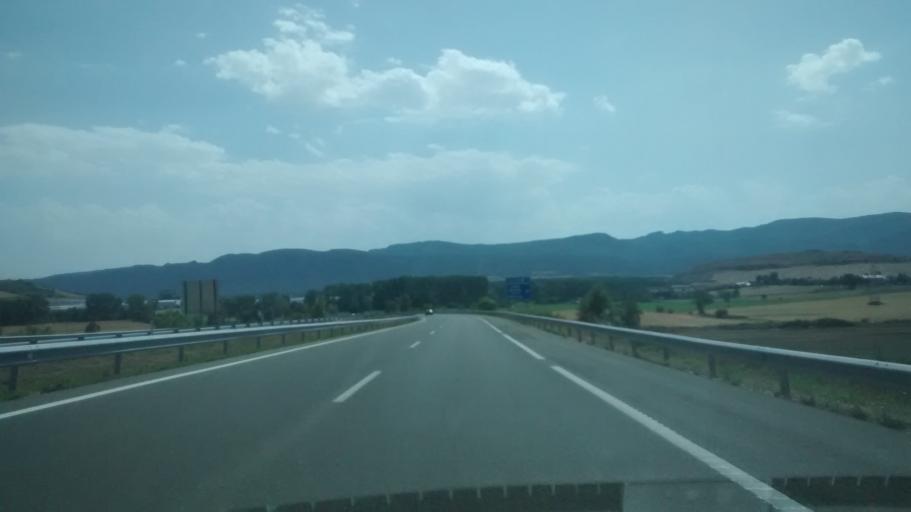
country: ES
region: Basque Country
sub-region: Provincia de Alava
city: Zambrana
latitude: 42.6903
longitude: -2.8914
